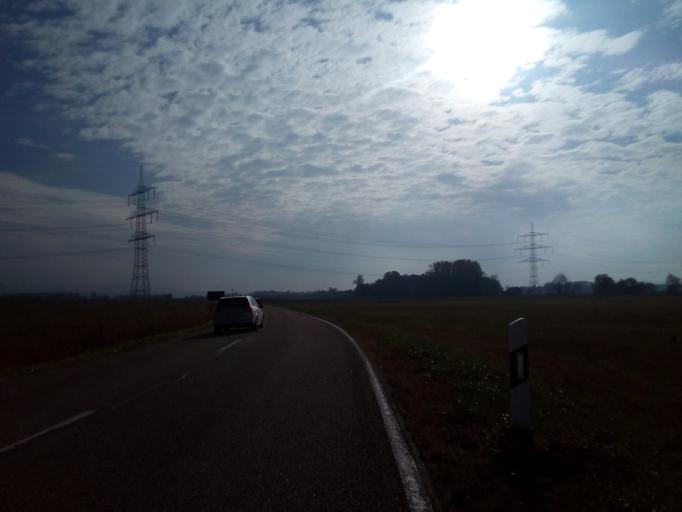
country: DE
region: Baden-Wuerttemberg
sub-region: Karlsruhe Region
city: Zell
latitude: 48.7111
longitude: 8.0685
